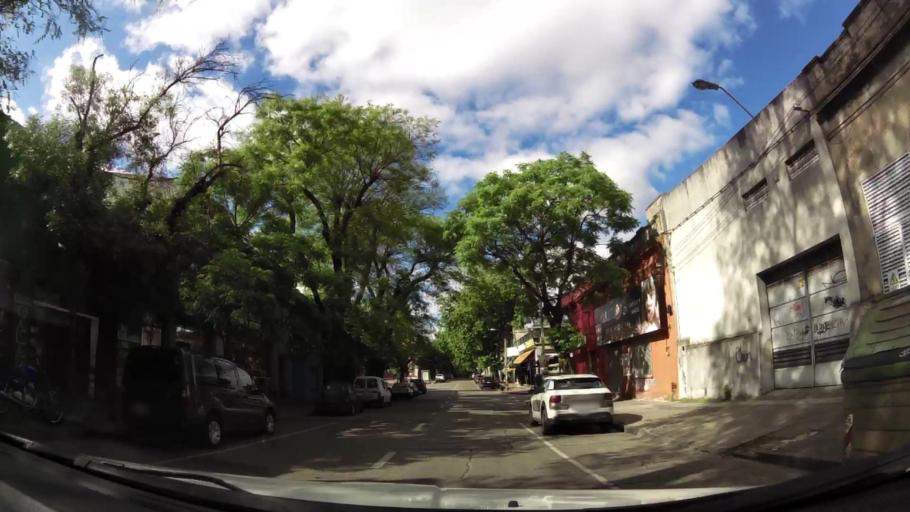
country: UY
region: Montevideo
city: Montevideo
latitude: -34.8820
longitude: -56.1777
